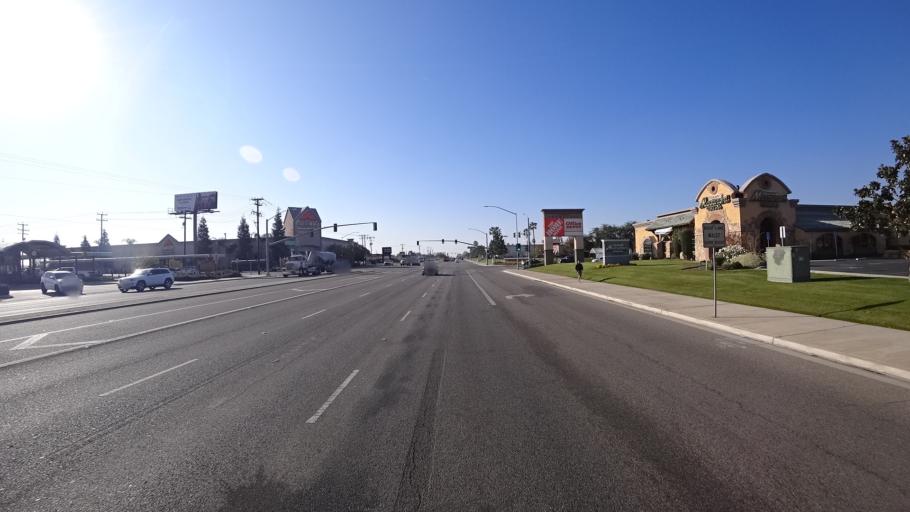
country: US
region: California
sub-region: Kern County
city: Greenacres
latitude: 35.3835
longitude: -119.1002
